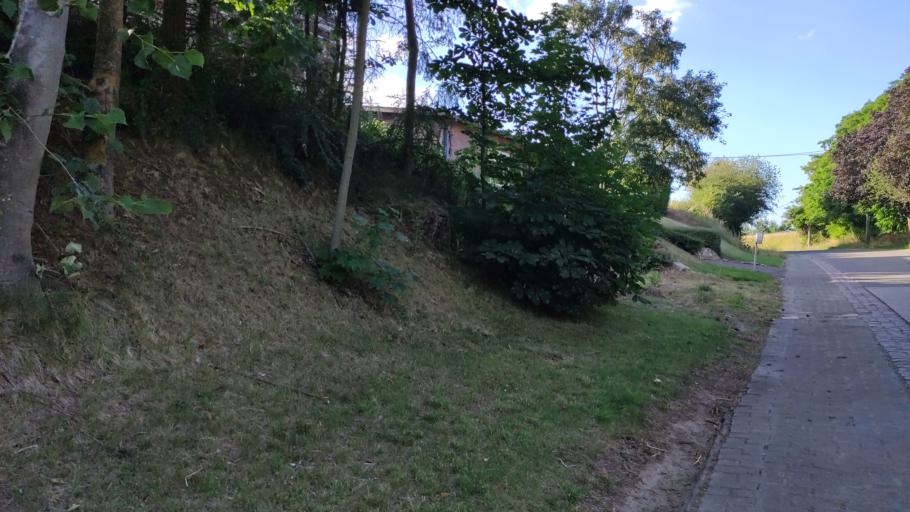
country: BE
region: Flanders
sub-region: Provincie Vlaams-Brabant
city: Hoegaarden
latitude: 50.7676
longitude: 4.8880
